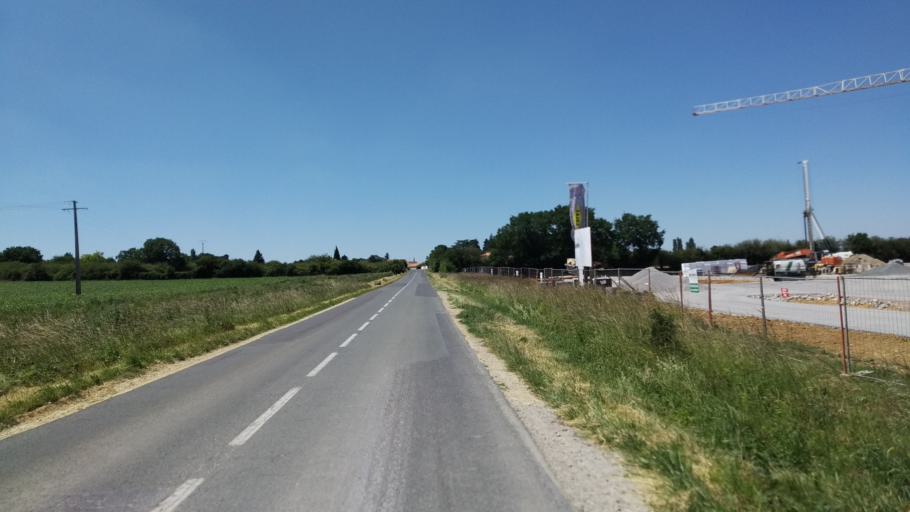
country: FR
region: Poitou-Charentes
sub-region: Departement de la Vienne
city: Biard
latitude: 46.6001
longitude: 0.2911
